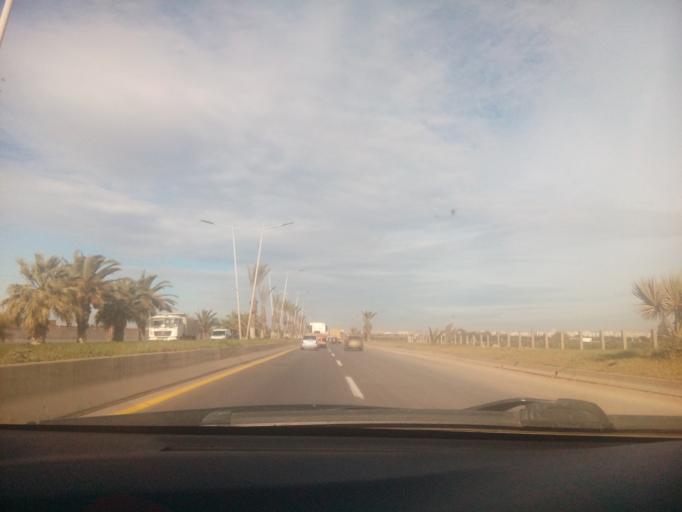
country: DZ
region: Oran
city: Es Senia
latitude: 35.6551
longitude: -0.5921
